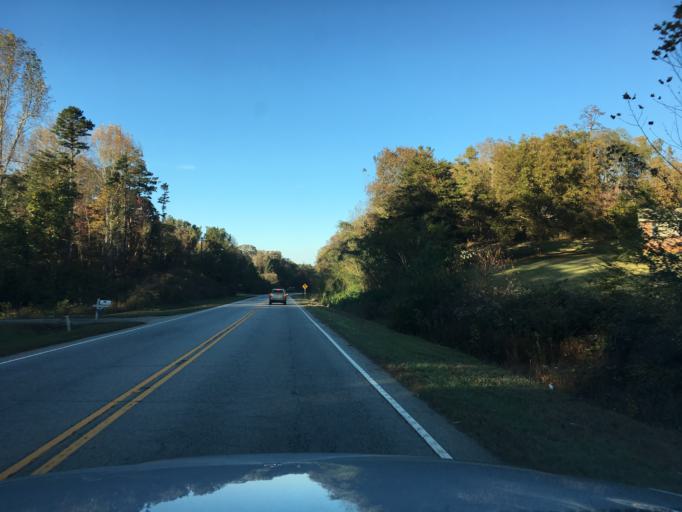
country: US
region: South Carolina
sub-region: Oconee County
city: Utica
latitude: 34.7175
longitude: -82.9224
